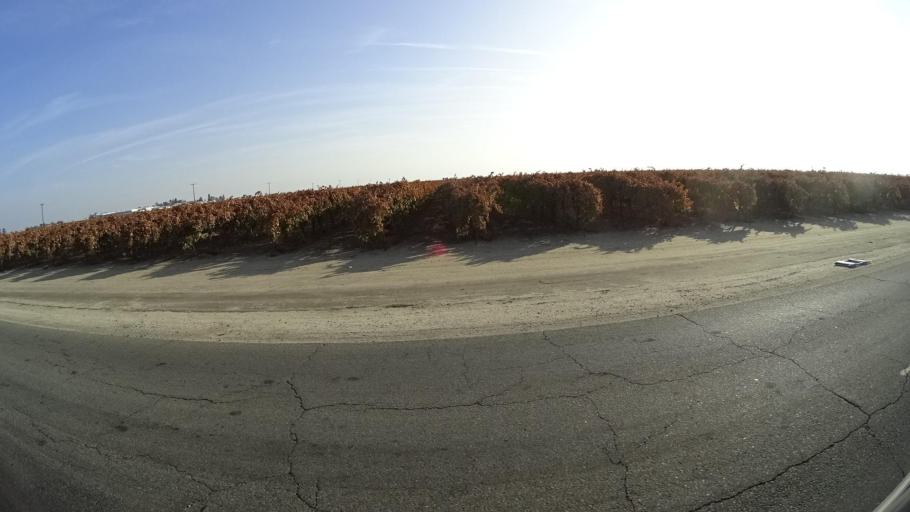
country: US
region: California
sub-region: Kern County
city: Delano
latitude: 35.7677
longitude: -119.1875
